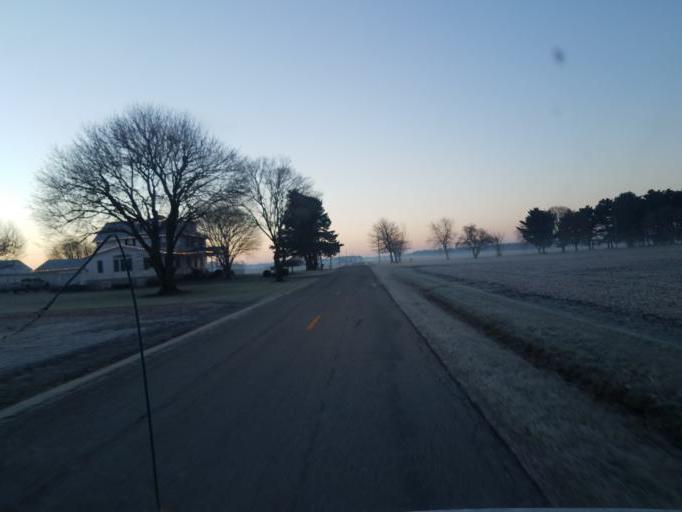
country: US
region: Ohio
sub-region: Marion County
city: Marion
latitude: 40.5736
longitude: -83.0196
